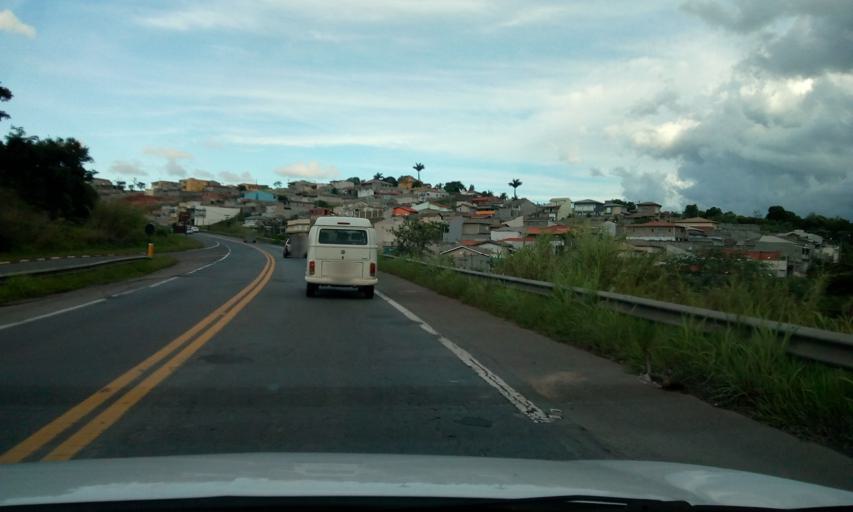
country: BR
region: Sao Paulo
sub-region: Itatiba
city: Itatiba
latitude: -23.0148
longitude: -46.8247
